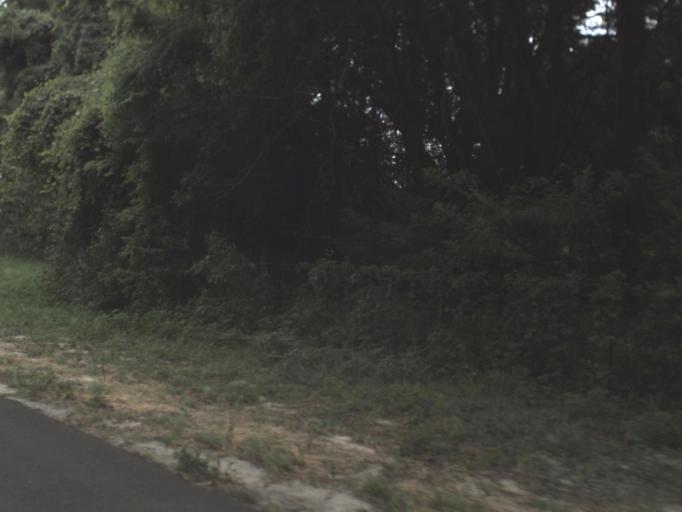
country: US
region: Florida
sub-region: Alachua County
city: Archer
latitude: 29.5088
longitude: -82.5026
